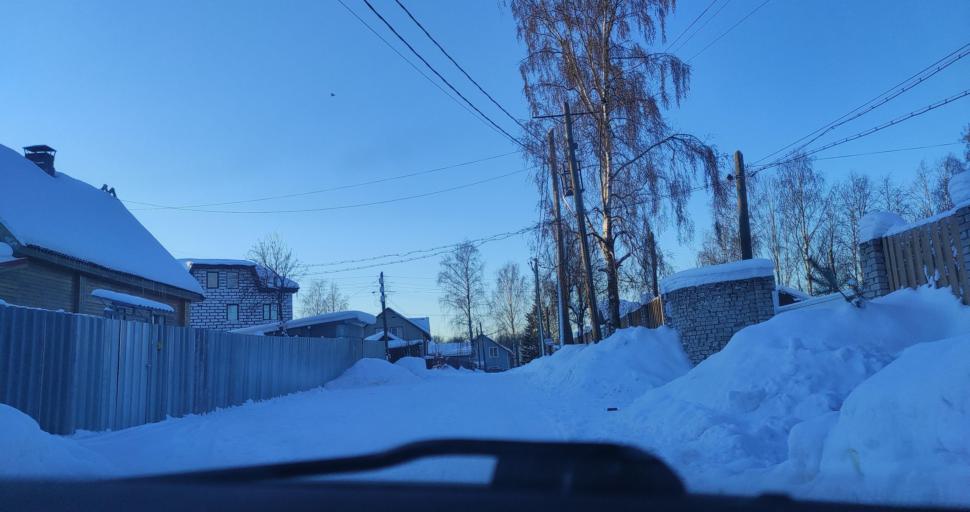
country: RU
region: Republic of Karelia
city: Petrozavodsk
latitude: 61.7879
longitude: 34.3169
